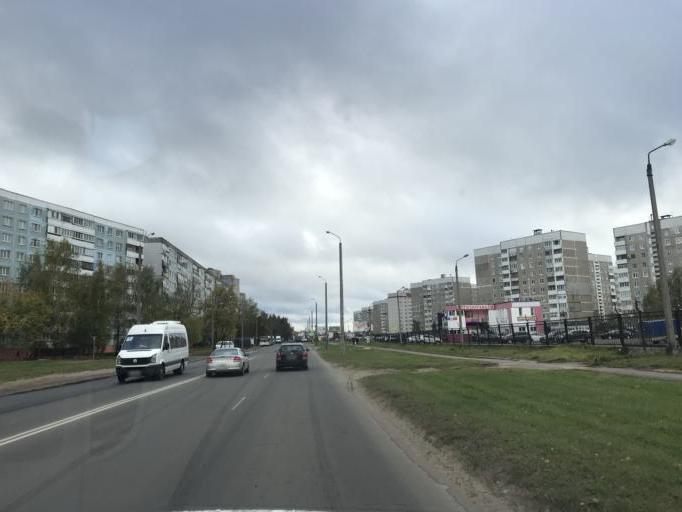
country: BY
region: Mogilev
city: Mahilyow
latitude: 53.8789
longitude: 30.3689
